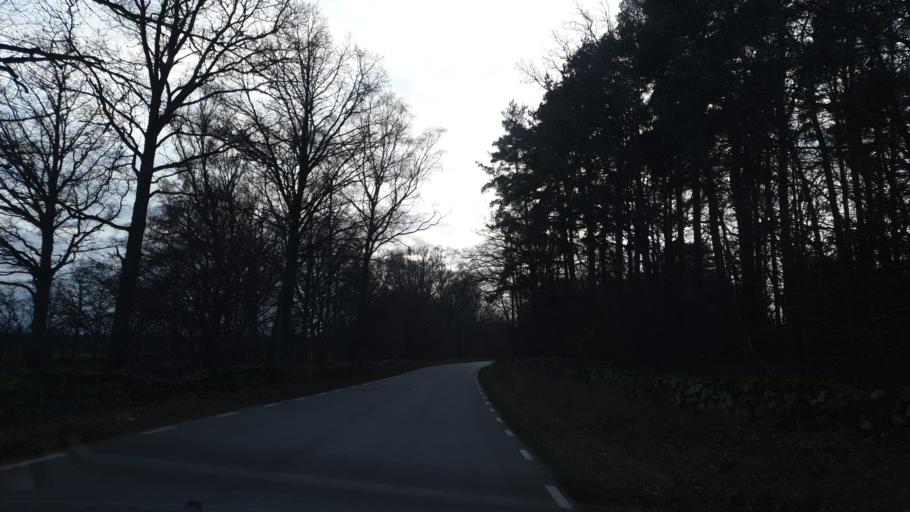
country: SE
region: Blekinge
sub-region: Karlskrona Kommun
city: Jaemjoe
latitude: 56.2023
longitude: 15.9569
